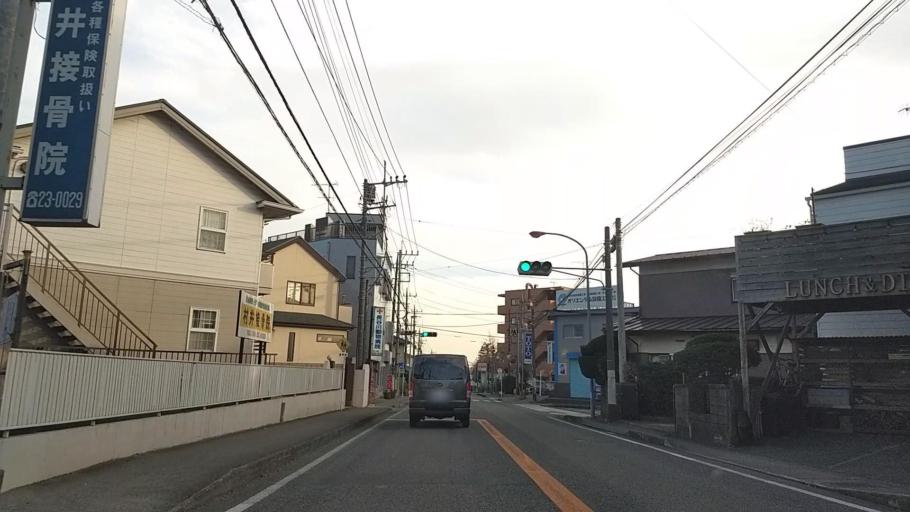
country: JP
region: Kanagawa
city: Atsugi
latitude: 35.4672
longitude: 139.3524
